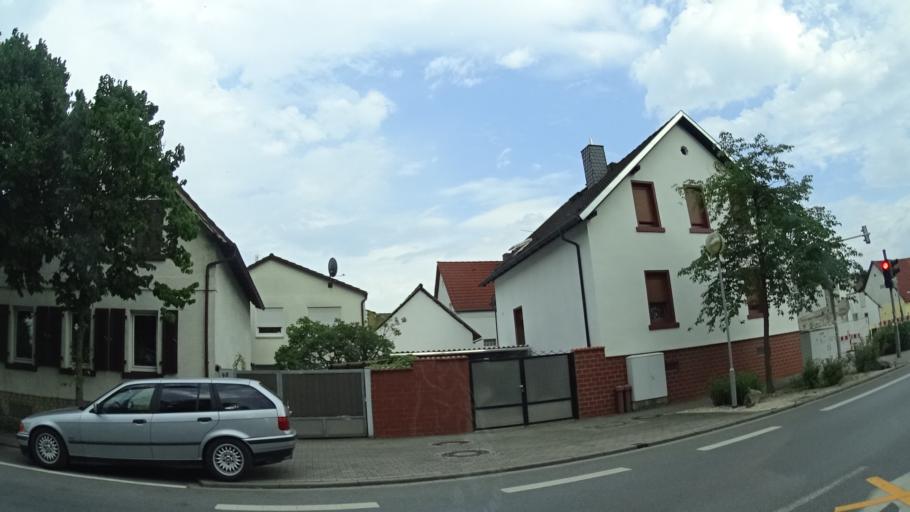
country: DE
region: Hesse
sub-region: Regierungsbezirk Darmstadt
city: Seeheim-Jugenheim
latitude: 49.7690
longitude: 8.6451
